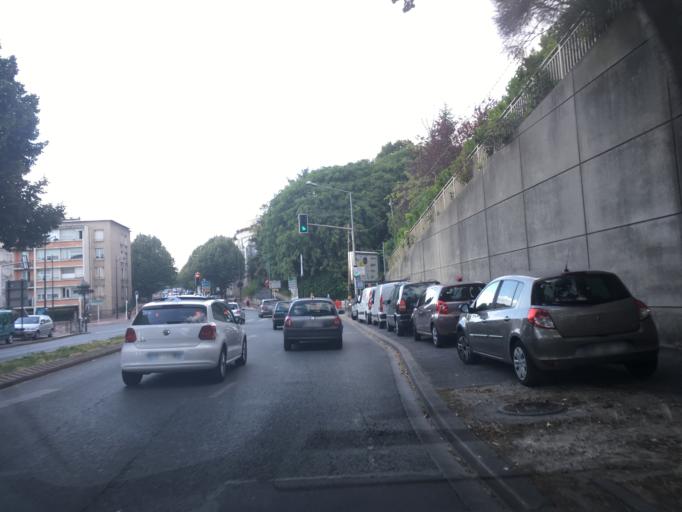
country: FR
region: Ile-de-France
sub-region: Departement du Val-de-Marne
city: Joinville-le-Pont
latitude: 48.8145
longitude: 2.4639
